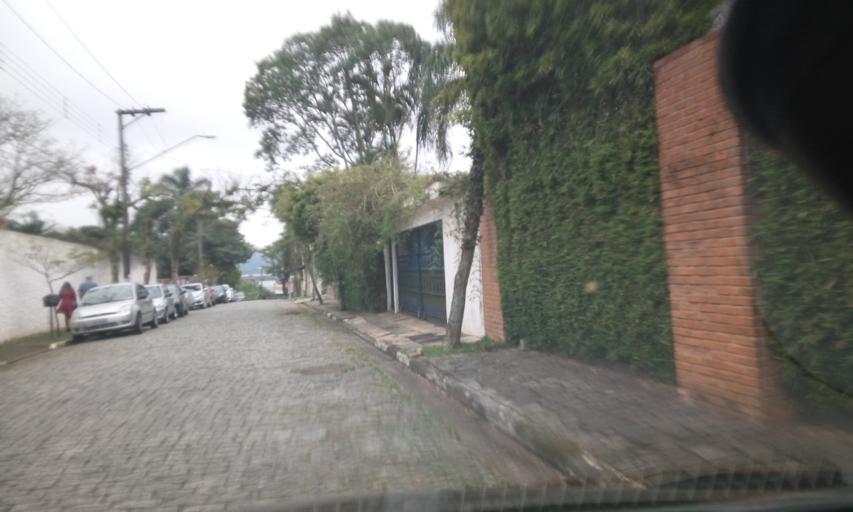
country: BR
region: Sao Paulo
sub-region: Sao Bernardo Do Campo
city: Sao Bernardo do Campo
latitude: -23.7796
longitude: -46.5360
